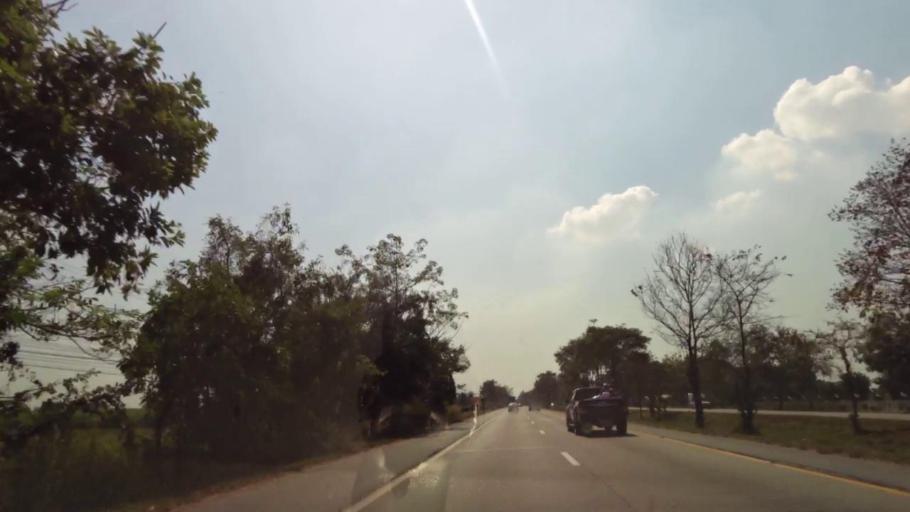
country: TH
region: Phichit
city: Wachira Barami
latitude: 16.5501
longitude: 100.1465
